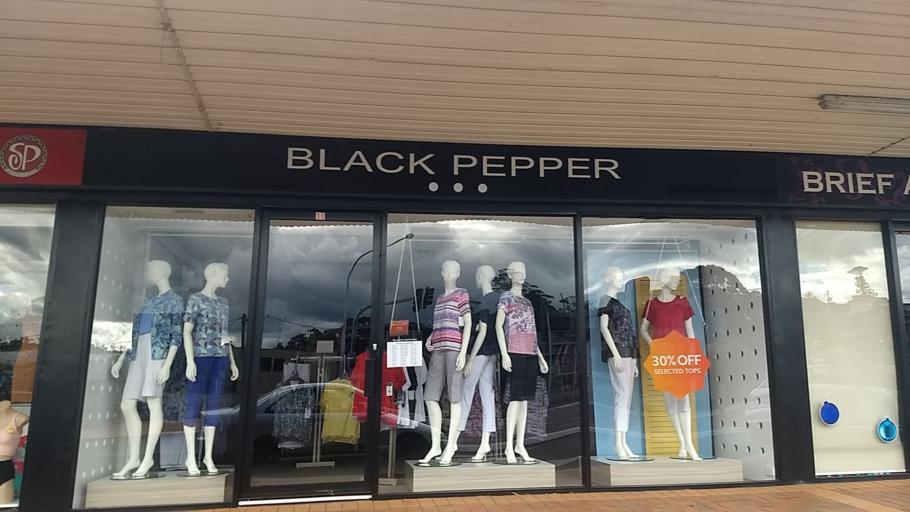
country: AU
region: New South Wales
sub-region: Bega Valley
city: Merimbula
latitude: -36.8893
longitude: 149.9107
